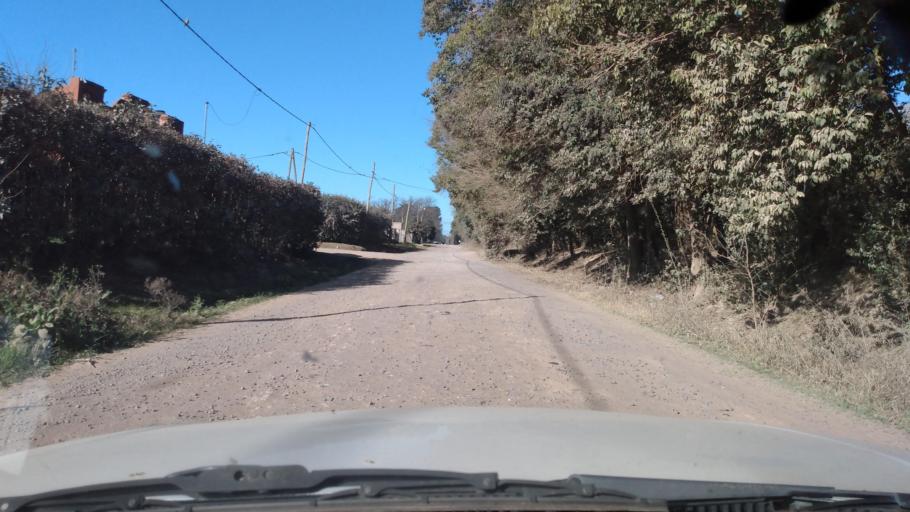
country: AR
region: Buenos Aires
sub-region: Partido de Mercedes
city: Mercedes
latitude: -34.6491
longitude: -59.4075
